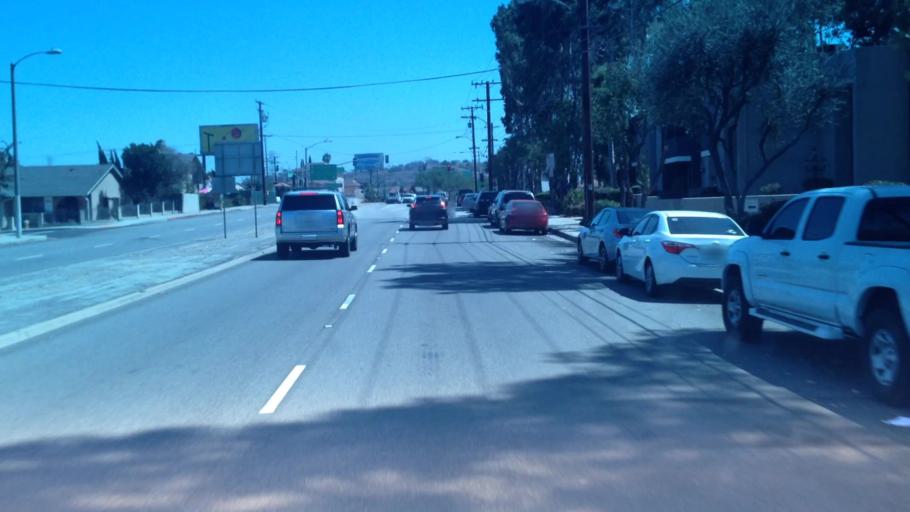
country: US
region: California
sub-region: Los Angeles County
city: South San Gabriel
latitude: 34.0461
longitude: -118.0906
